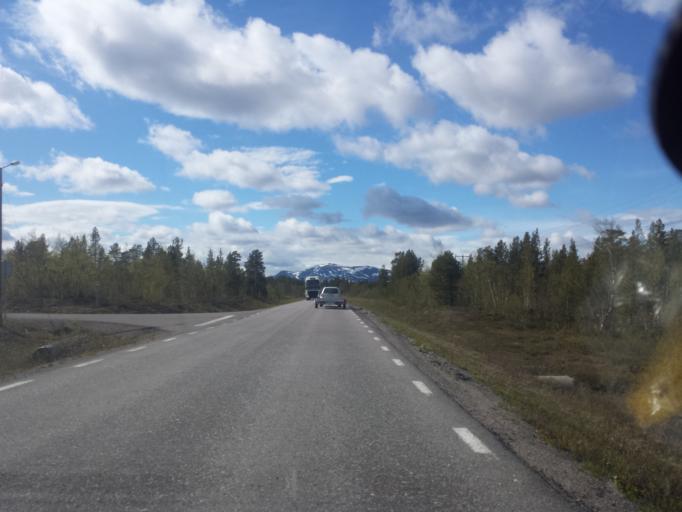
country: SE
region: Norrbotten
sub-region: Kiruna Kommun
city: Kiruna
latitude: 67.9926
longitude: 19.9137
